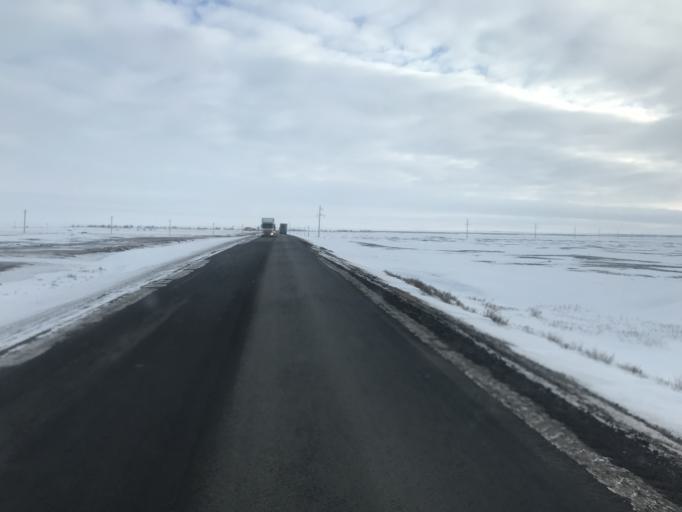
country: RU
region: Orenburg
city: Dombarovskiy
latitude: 49.9406
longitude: 60.1100
